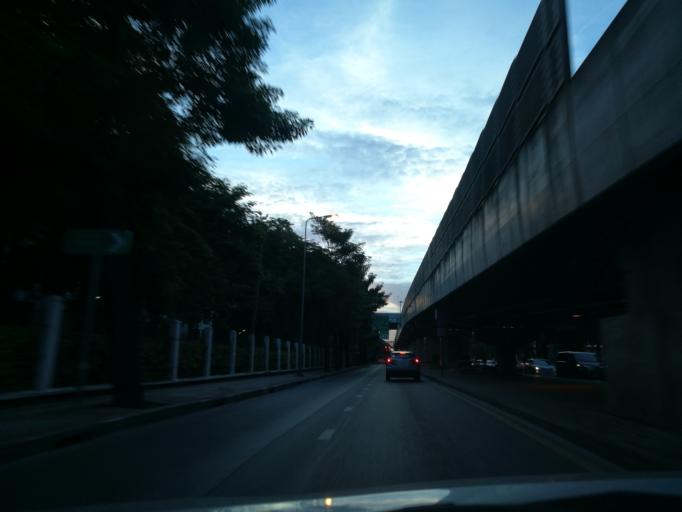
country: TH
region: Bangkok
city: Ratchathewi
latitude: 13.7684
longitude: 100.5308
